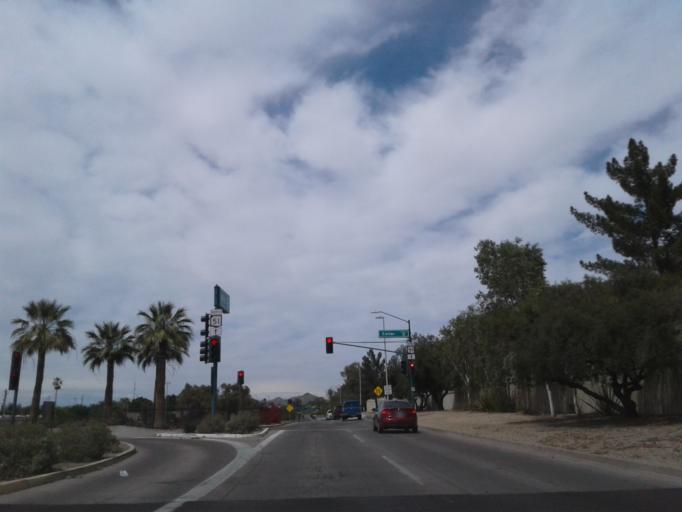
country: US
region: Arizona
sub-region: Maricopa County
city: Phoenix
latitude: 33.5125
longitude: -112.0437
